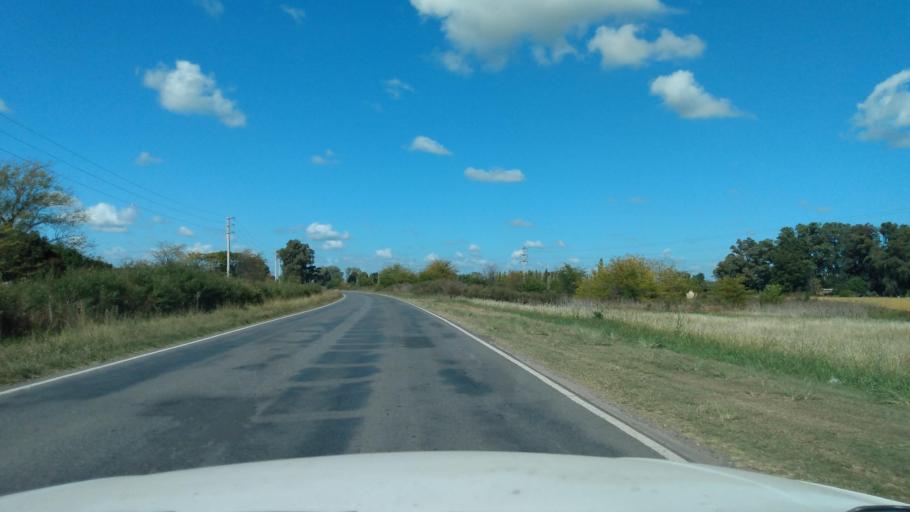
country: AR
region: Buenos Aires
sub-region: Partido de Mercedes
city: Mercedes
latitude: -34.7025
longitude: -59.4028
